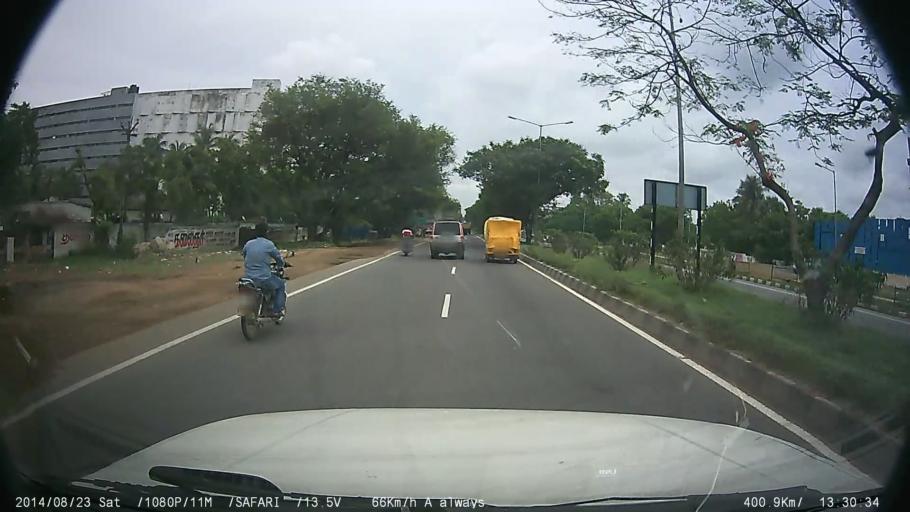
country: IN
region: Tamil Nadu
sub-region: Kancheepuram
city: Vandalur
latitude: 12.8733
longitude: 80.0777
